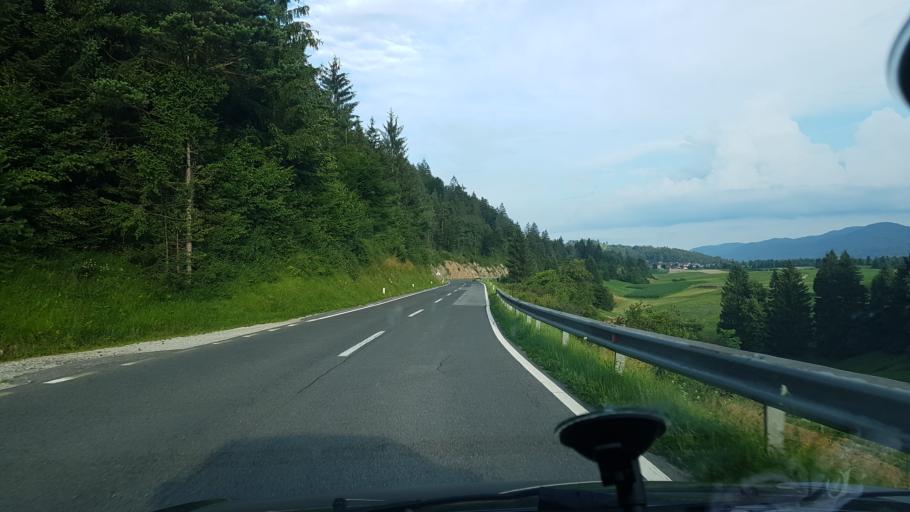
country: SI
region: Ziri
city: Ziri
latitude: 45.9419
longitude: 14.1219
